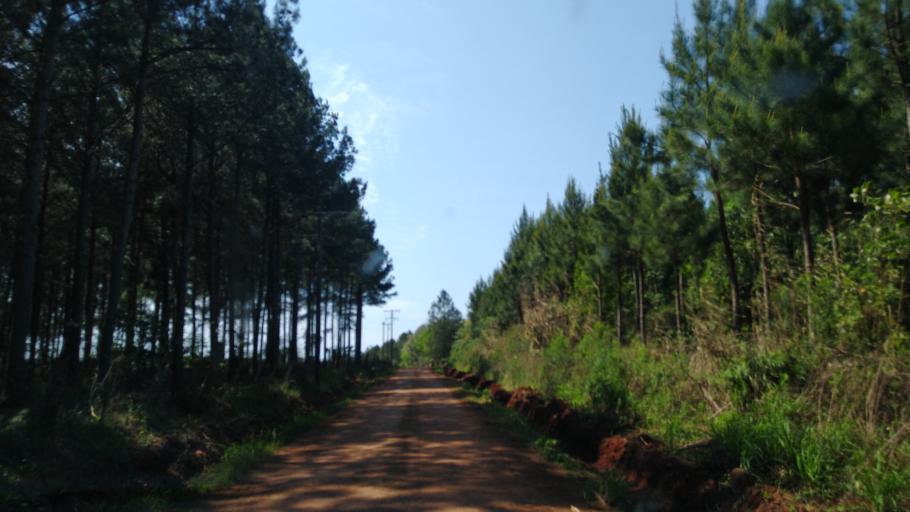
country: AR
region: Misiones
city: Capiovi
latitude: -26.9433
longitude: -55.0558
